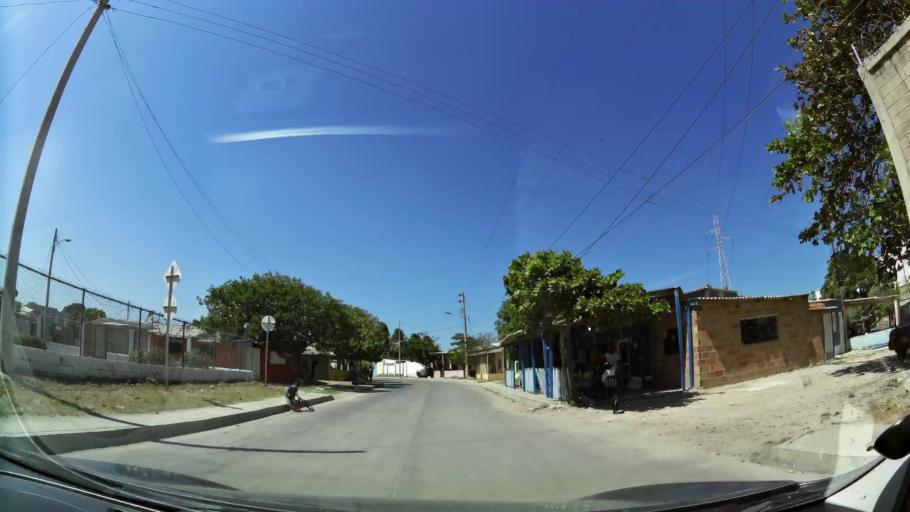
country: CO
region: Atlantico
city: Barranquilla
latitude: 10.9803
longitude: -74.7626
